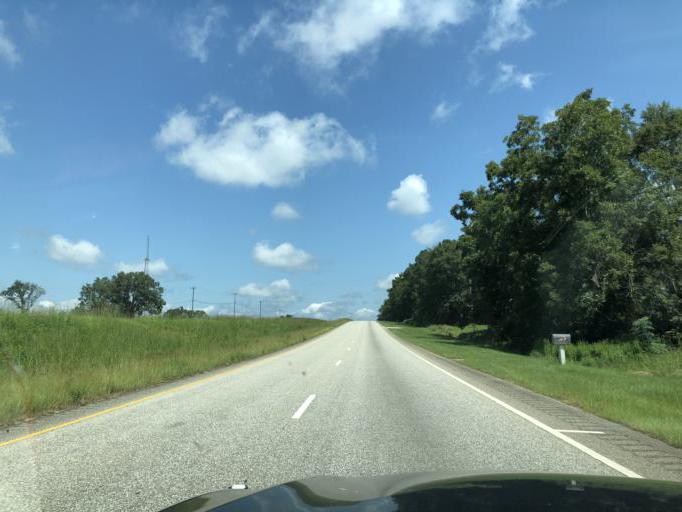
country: US
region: Alabama
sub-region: Henry County
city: Abbeville
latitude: 31.7083
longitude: -85.2746
